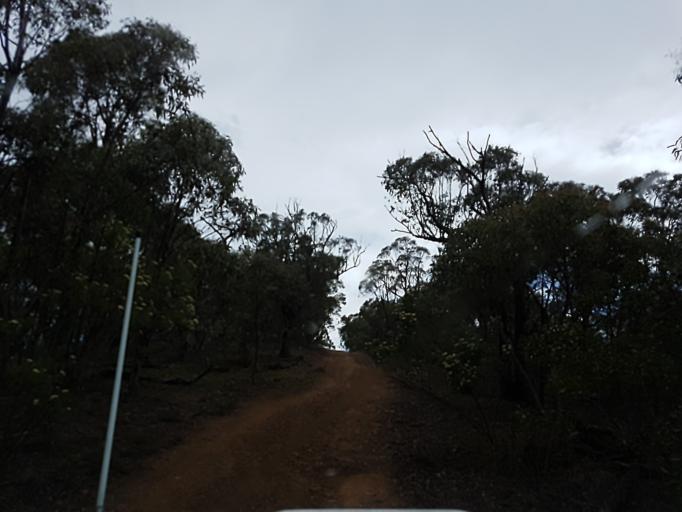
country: AU
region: New South Wales
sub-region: Snowy River
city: Jindabyne
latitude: -36.9074
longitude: 148.3401
